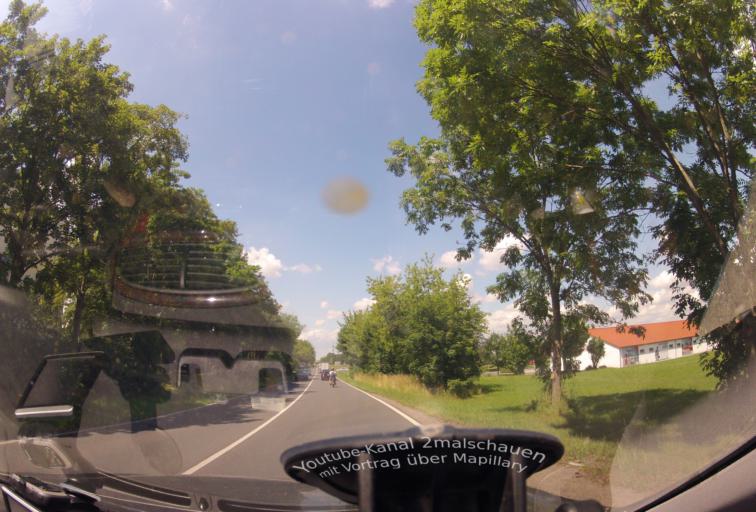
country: DE
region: Saxony
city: Torgau
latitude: 51.5668
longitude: 12.9758
